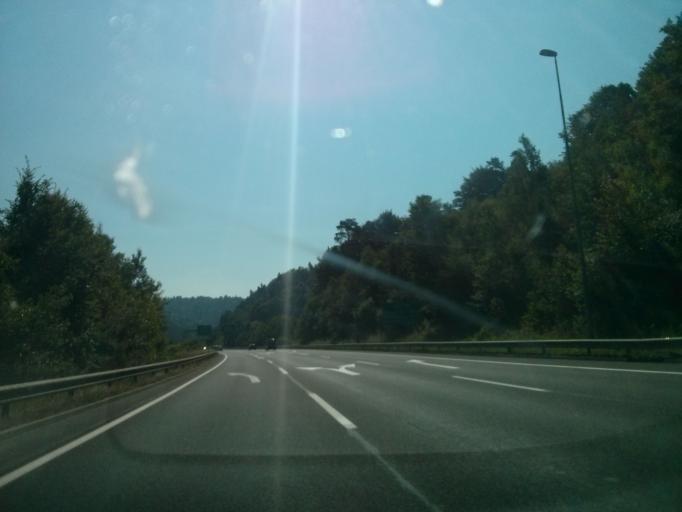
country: SI
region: Skofljica
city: Lavrica
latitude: 46.0128
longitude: 14.5514
